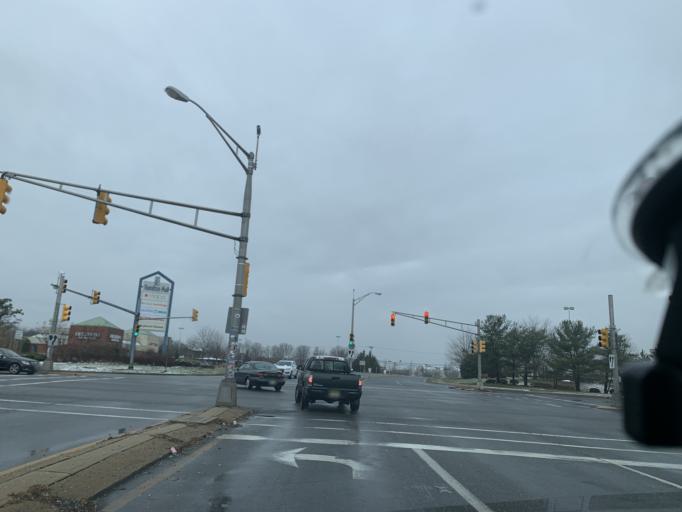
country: US
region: New Jersey
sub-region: Atlantic County
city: Pomona
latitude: 39.4500
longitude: -74.6374
